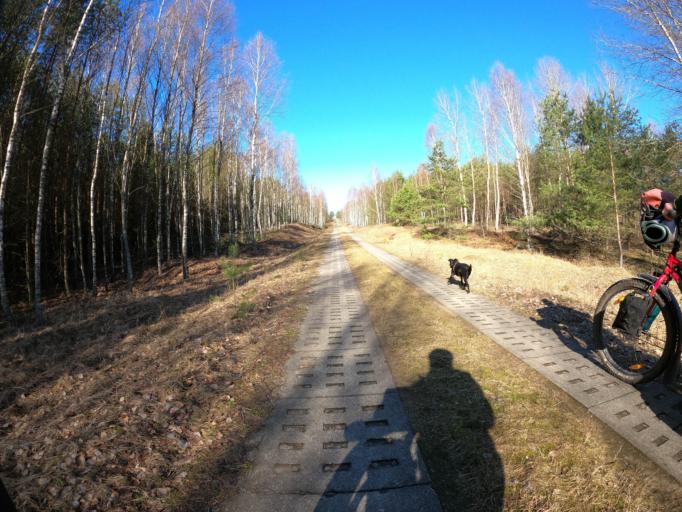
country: PL
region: Greater Poland Voivodeship
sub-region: Powiat zlotowski
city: Sypniewo
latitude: 53.5258
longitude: 16.6322
